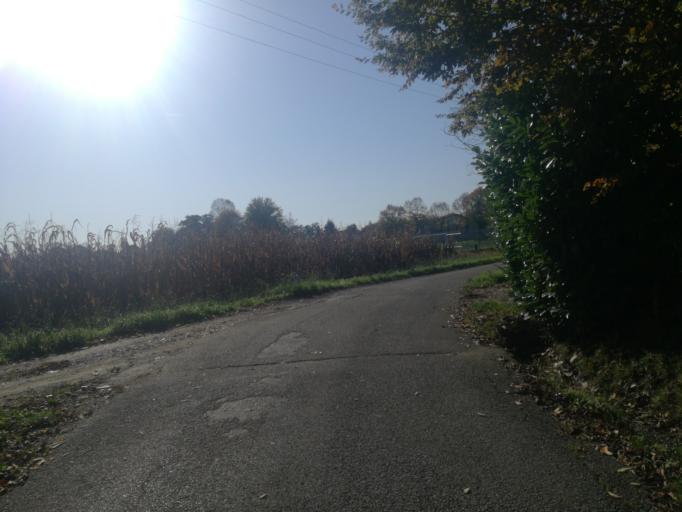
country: IT
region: Lombardy
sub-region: Provincia di Monza e Brianza
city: Porto d'Adda
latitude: 45.6515
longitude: 9.4734
